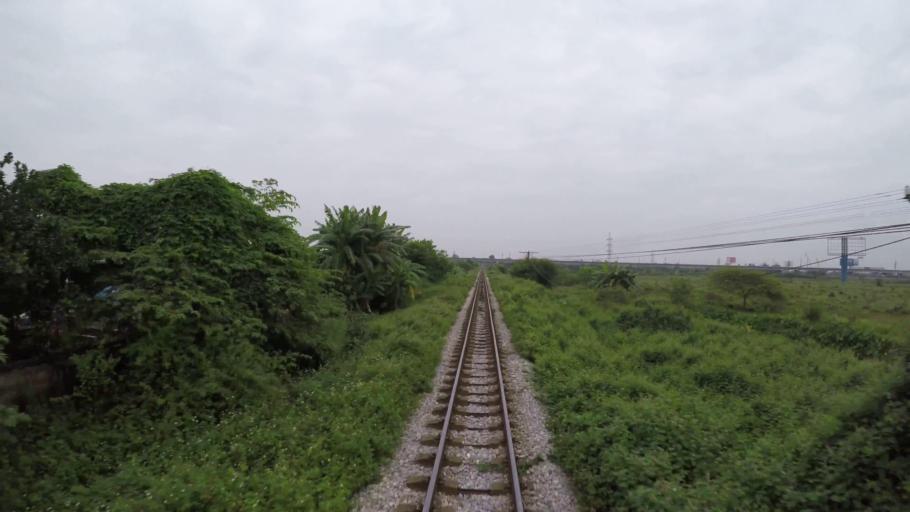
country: VN
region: Hai Phong
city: An Duong
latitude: 20.9109
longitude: 106.5697
